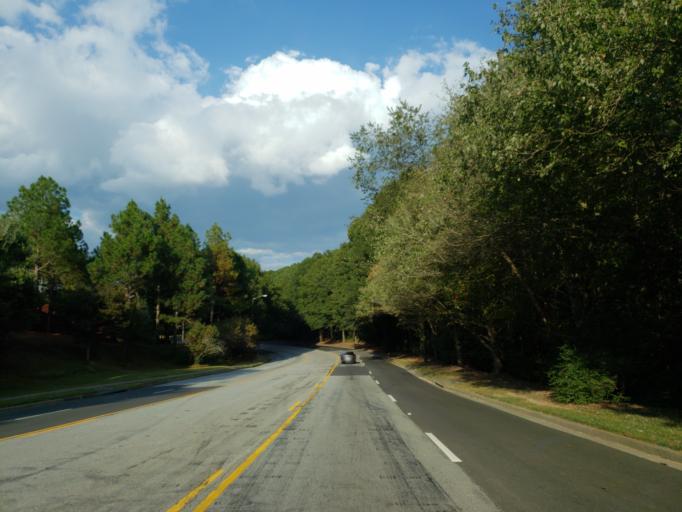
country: US
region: Georgia
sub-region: Cobb County
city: Mableton
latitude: 33.7639
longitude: -84.5604
